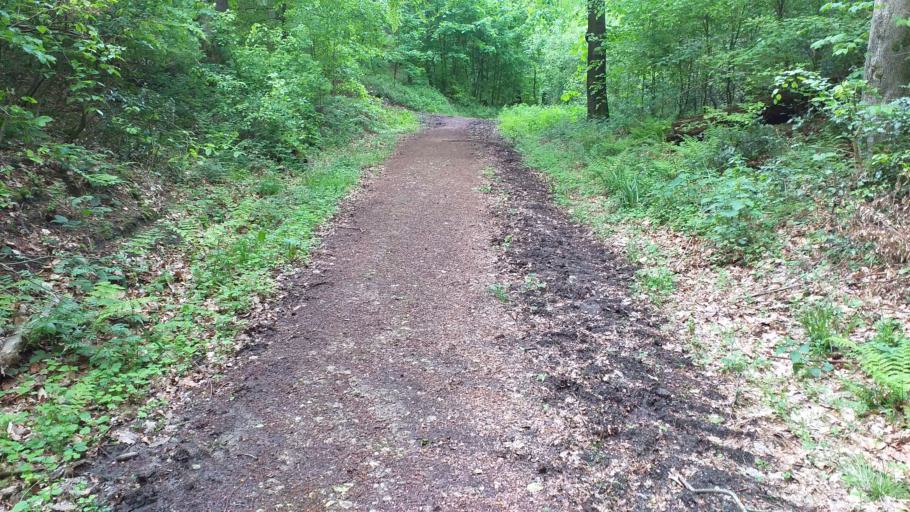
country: DE
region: North Rhine-Westphalia
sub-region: Regierungsbezirk Koln
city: Aachen
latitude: 50.7346
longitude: 6.0853
